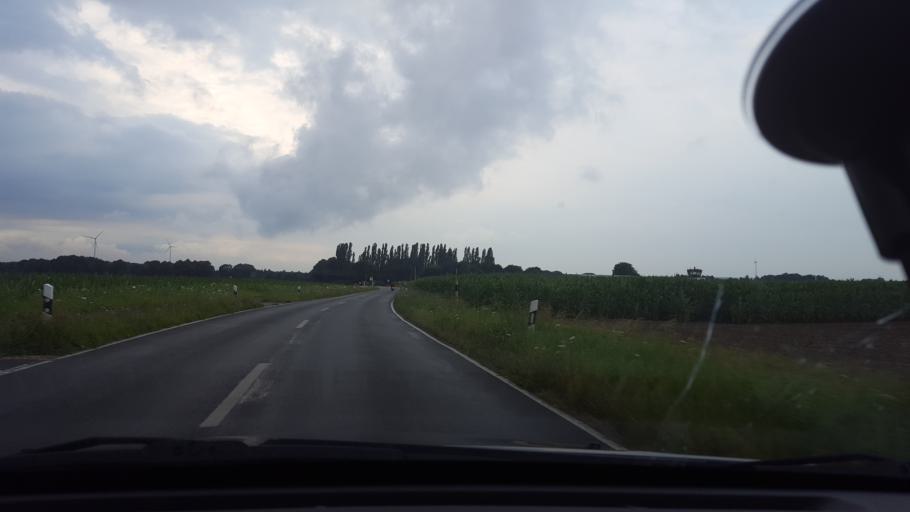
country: DE
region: North Rhine-Westphalia
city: Herten
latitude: 51.6444
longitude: 7.1562
